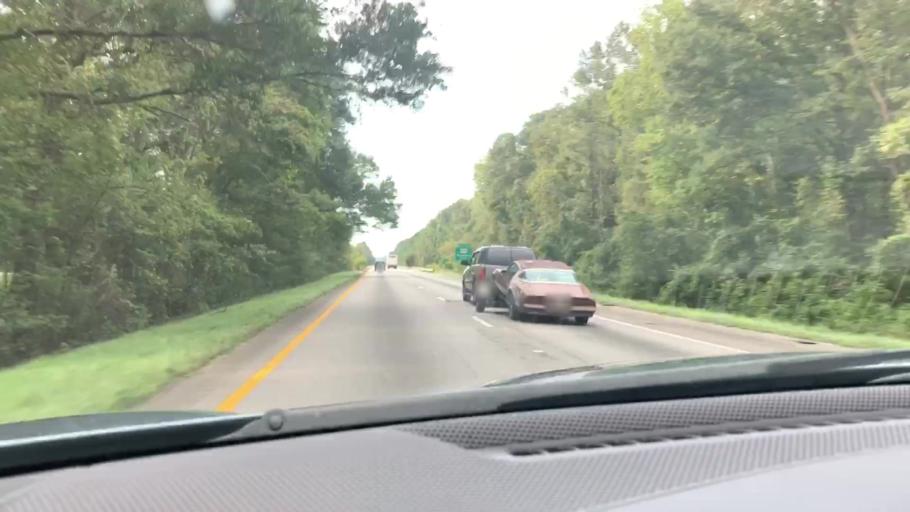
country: US
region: South Carolina
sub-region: Dorchester County
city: Saint George
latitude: 33.3455
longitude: -80.5764
